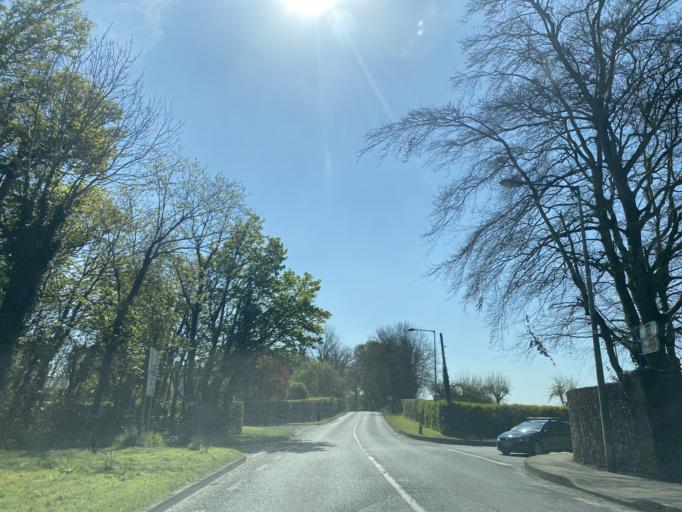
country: IE
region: Leinster
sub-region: Kildare
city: Kill
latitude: 53.3041
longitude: -6.6139
